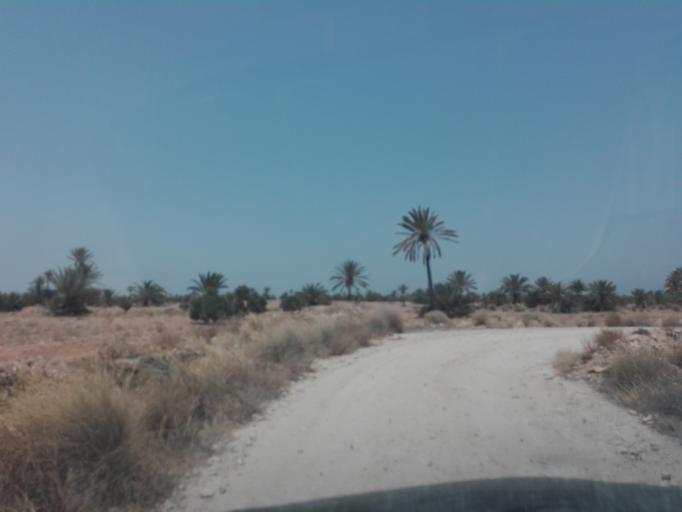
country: TN
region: Safaqis
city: Al Qarmadah
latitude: 34.6596
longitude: 11.0996
